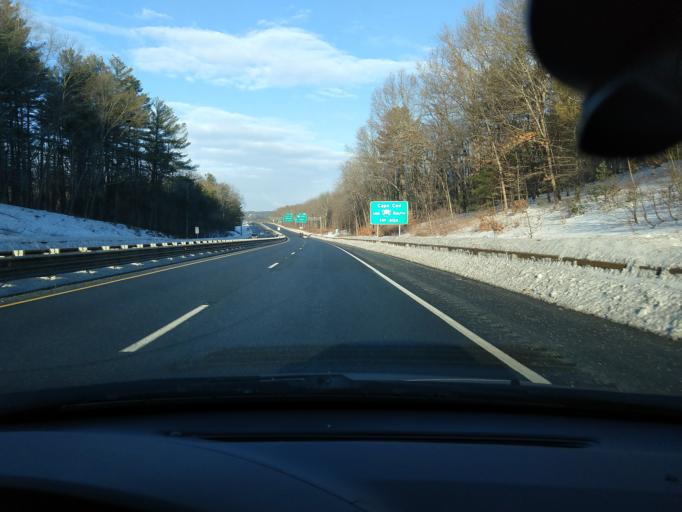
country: US
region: Massachusetts
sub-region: Middlesex County
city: Littleton Common
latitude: 42.5146
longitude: -71.4954
